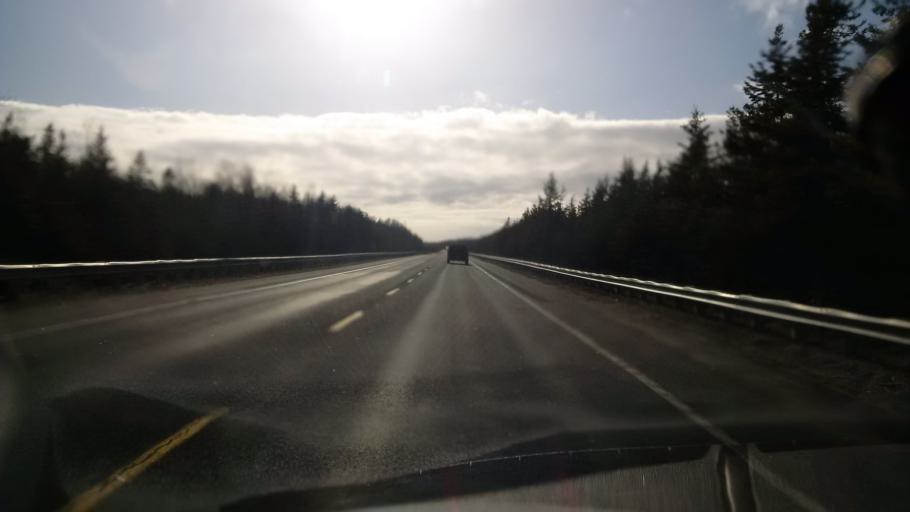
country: CA
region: Nova Scotia
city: Antigonish
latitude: 45.5872
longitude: -62.3090
